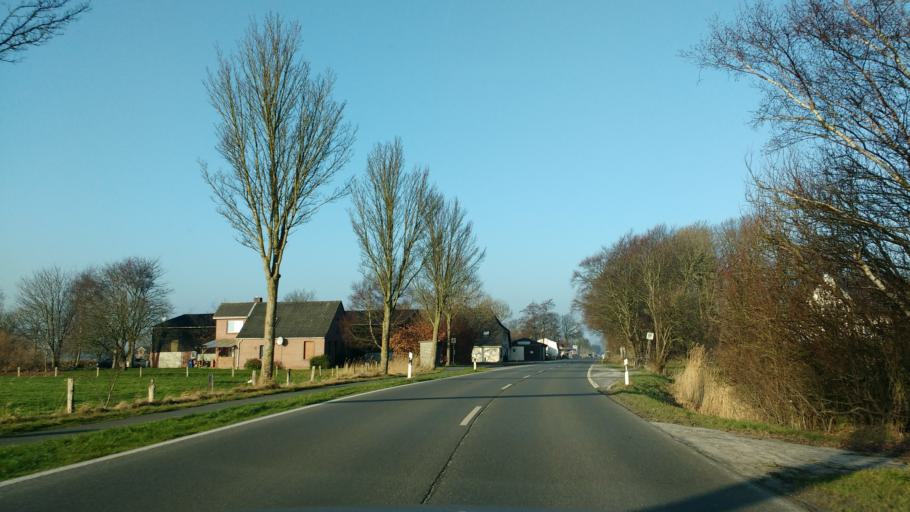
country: DE
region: Schleswig-Holstein
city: Kronprinzenkoog
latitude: 53.9897
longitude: 8.9435
